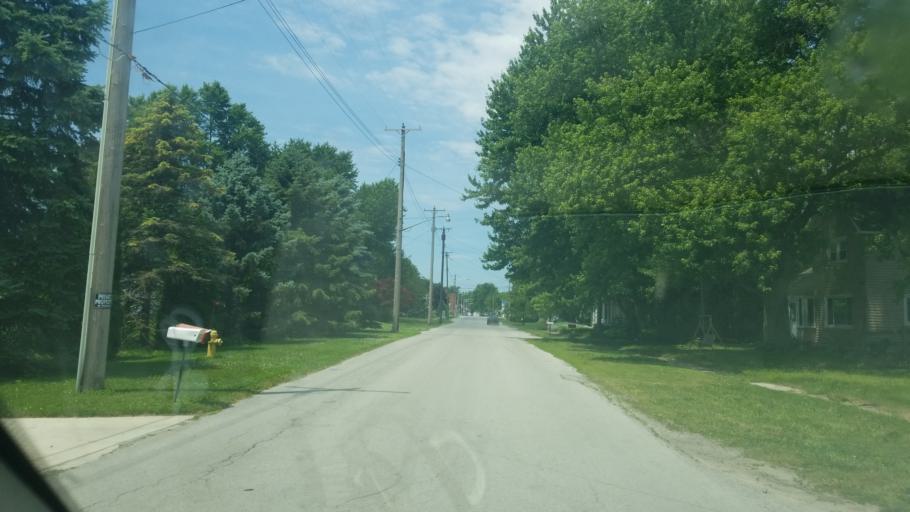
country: US
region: Ohio
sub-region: Wood County
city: North Baltimore
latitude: 41.2537
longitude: -83.6002
